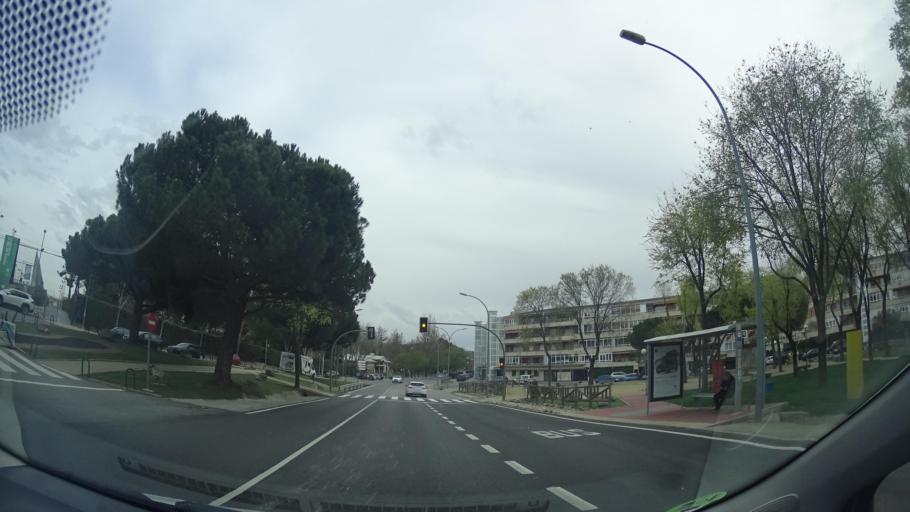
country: ES
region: Madrid
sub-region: Provincia de Madrid
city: Colmenar Viejo
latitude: 40.6733
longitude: -3.7701
